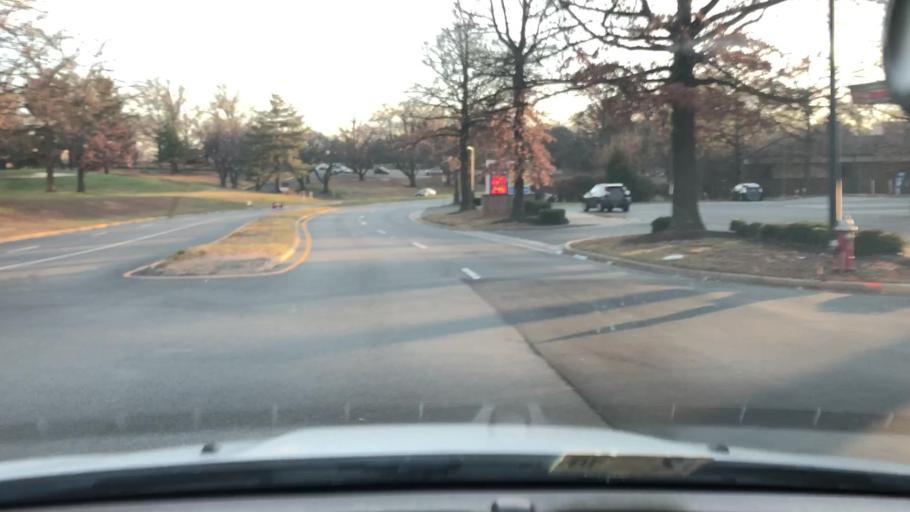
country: US
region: Virginia
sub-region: Fairfax County
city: Reston
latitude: 38.9474
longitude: -77.3566
